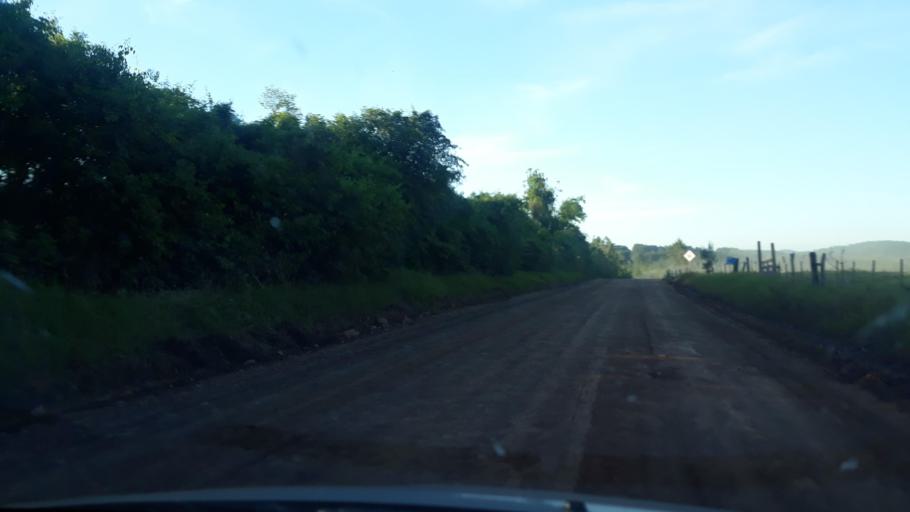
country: AR
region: Misiones
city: Ruiz de Montoya
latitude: -27.0494
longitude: -55.0040
